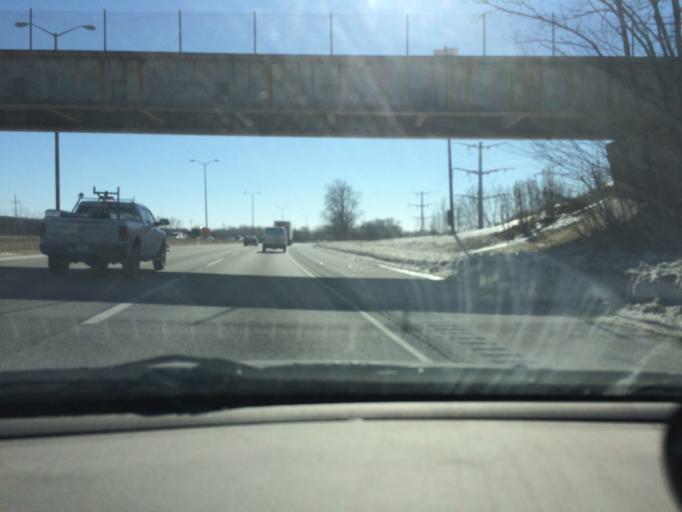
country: US
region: Illinois
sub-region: DuPage County
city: Lombard
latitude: 41.8818
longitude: -88.0334
